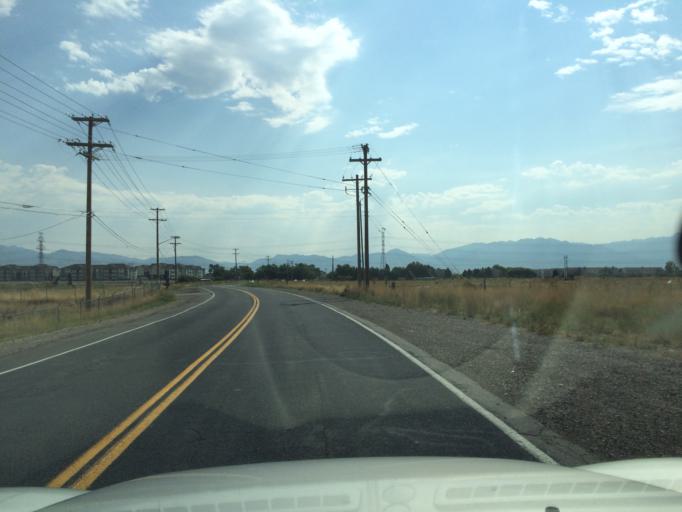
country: US
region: Utah
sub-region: Salt Lake County
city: West Valley City
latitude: 40.7104
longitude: -112.0355
